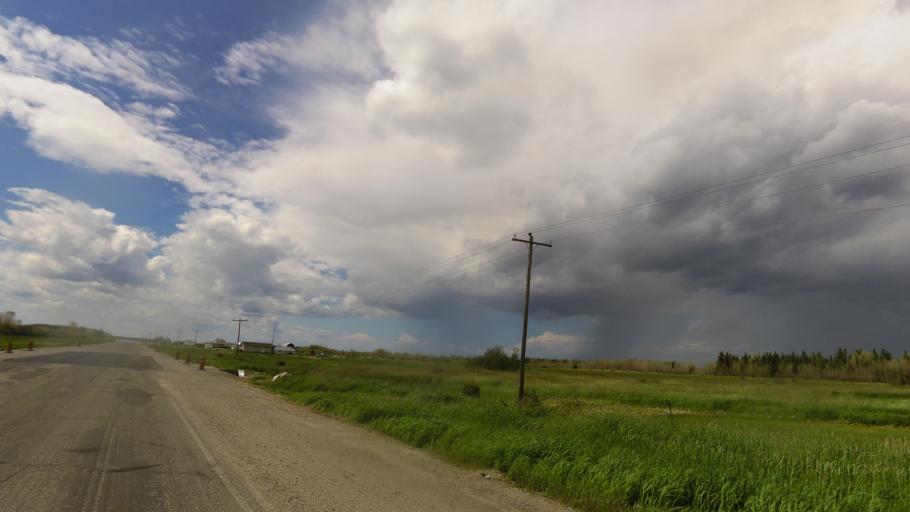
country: CA
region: Ontario
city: Hearst
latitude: 49.6036
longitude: -83.2247
